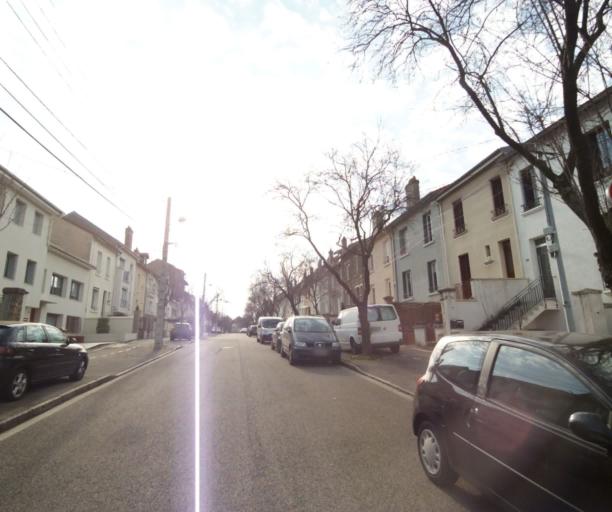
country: FR
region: Lorraine
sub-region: Departement de Meurthe-et-Moselle
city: Laxou
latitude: 48.6795
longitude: 6.1566
